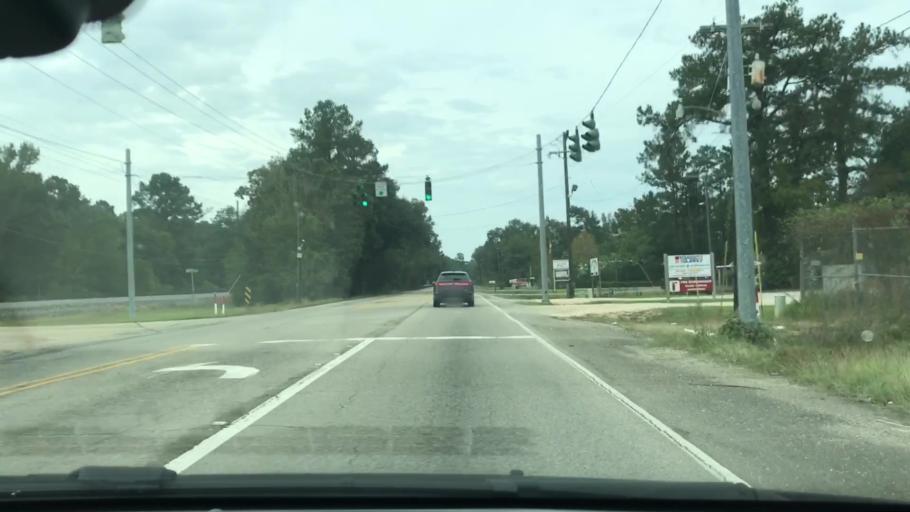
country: US
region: Louisiana
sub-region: Saint Tammany Parish
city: Slidell
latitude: 30.3017
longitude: -89.7740
